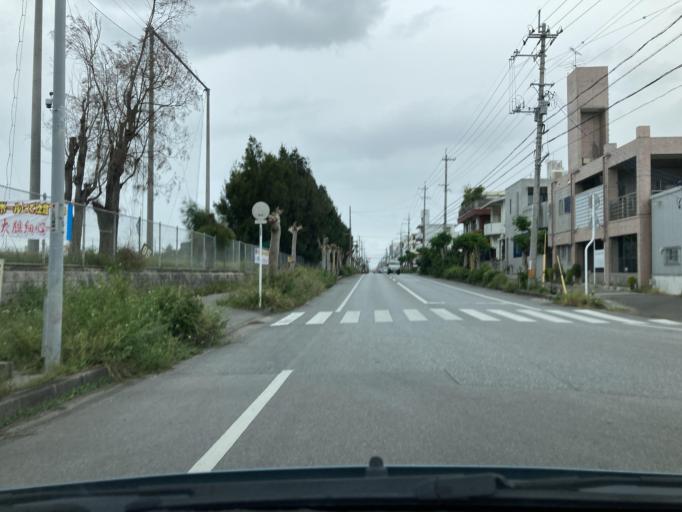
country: JP
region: Okinawa
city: Itoman
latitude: 26.1372
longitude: 127.6671
